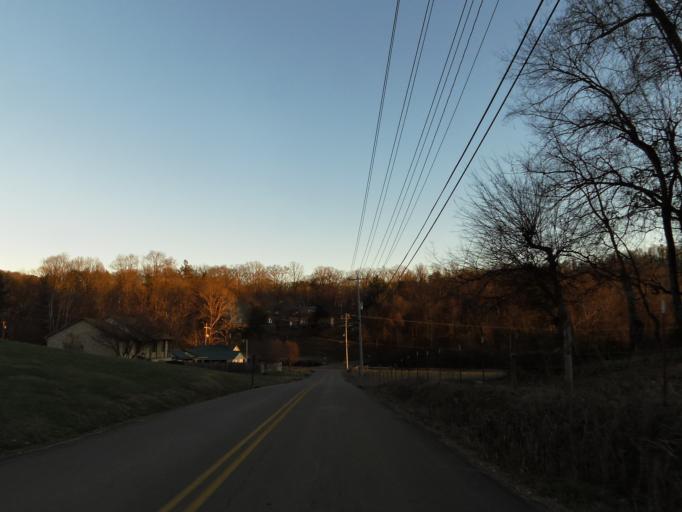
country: US
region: Tennessee
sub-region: Blount County
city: Eagleton Village
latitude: 35.8316
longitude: -83.9373
